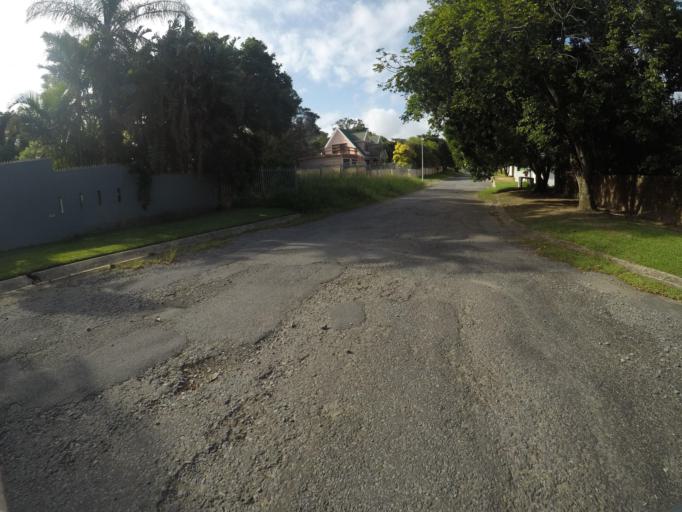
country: ZA
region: Eastern Cape
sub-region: Buffalo City Metropolitan Municipality
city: East London
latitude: -32.9714
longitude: 27.9565
